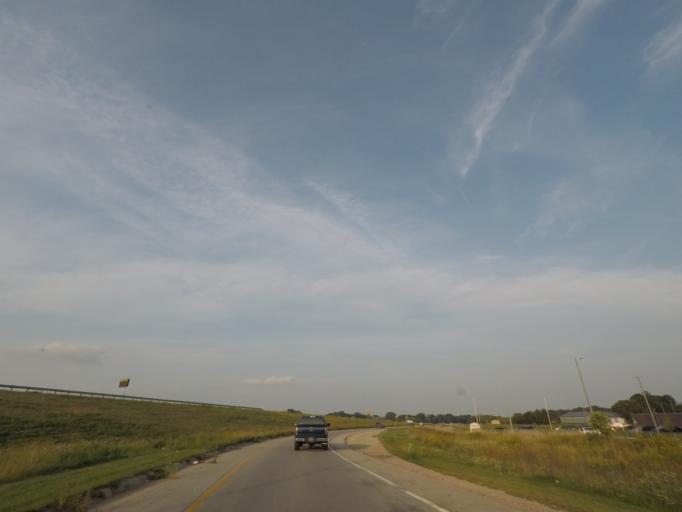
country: US
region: Wisconsin
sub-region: Dane County
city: Cottage Grove
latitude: 43.1088
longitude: -89.1988
